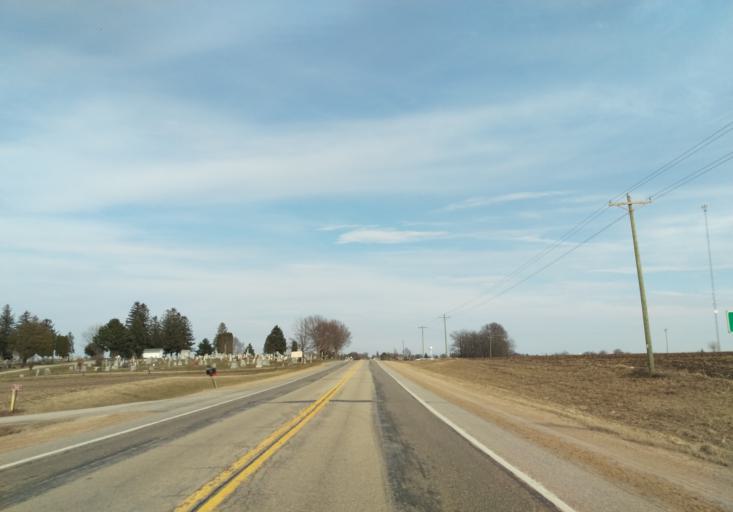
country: US
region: Wisconsin
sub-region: Grant County
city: Fennimore
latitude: 42.9884
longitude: -90.6785
